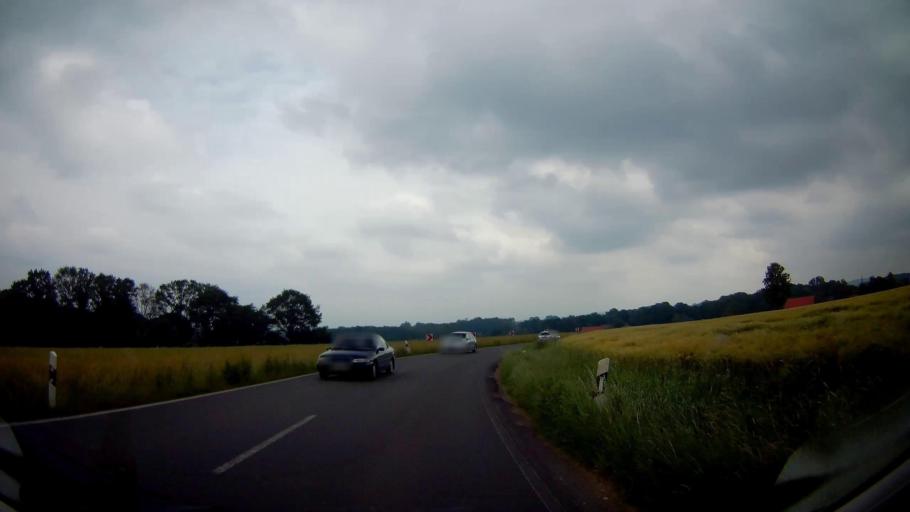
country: DE
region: North Rhine-Westphalia
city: Loehne
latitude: 52.1768
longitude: 8.7380
